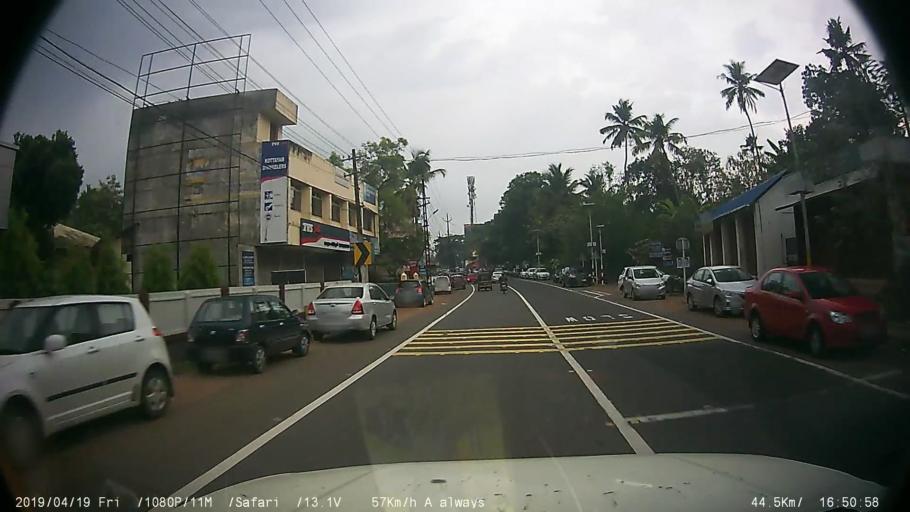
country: IN
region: Kerala
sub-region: Kottayam
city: Changanacheri
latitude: 9.4598
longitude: 76.5335
